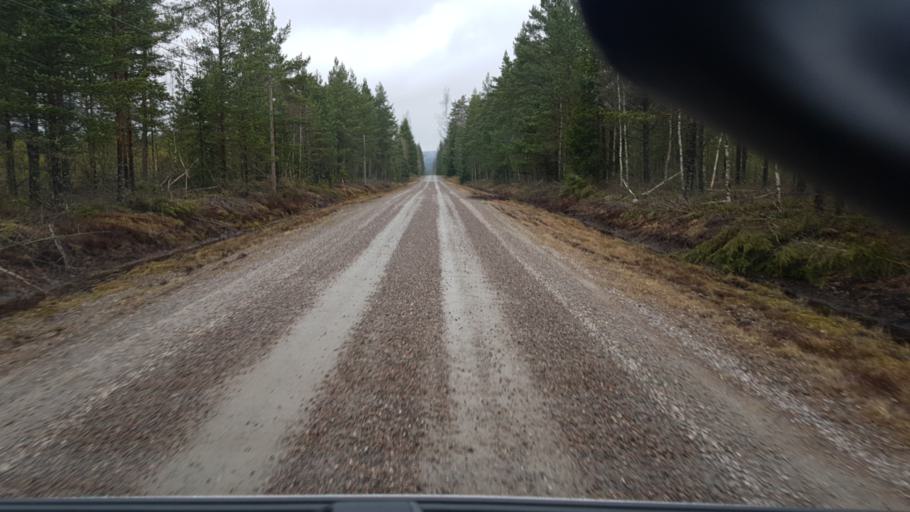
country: SE
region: Vaermland
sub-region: Eda Kommun
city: Charlottenberg
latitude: 59.9552
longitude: 12.5133
